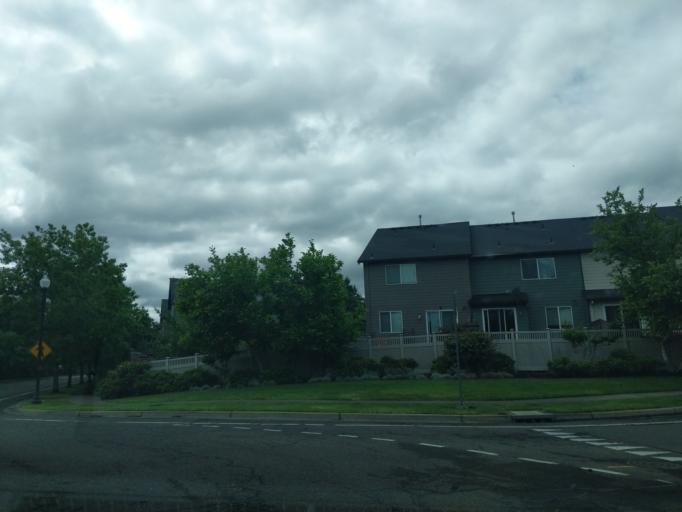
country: US
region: Oregon
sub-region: Yamhill County
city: Newberg
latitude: 45.3039
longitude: -122.9409
